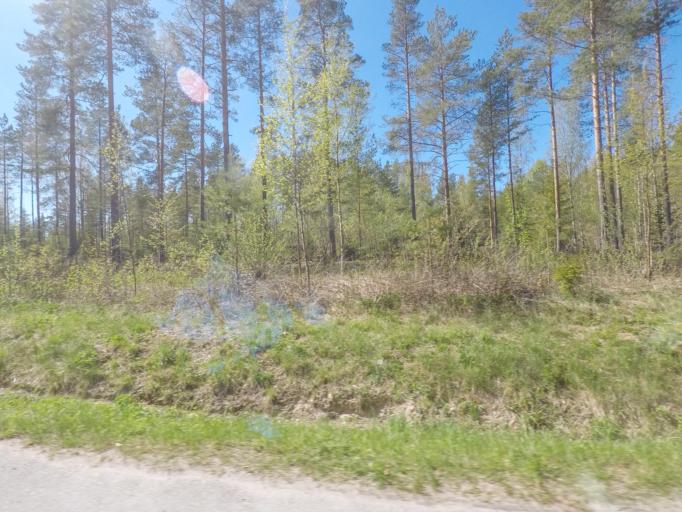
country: FI
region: Uusimaa
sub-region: Helsinki
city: Sammatti
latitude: 60.3295
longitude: 23.8133
